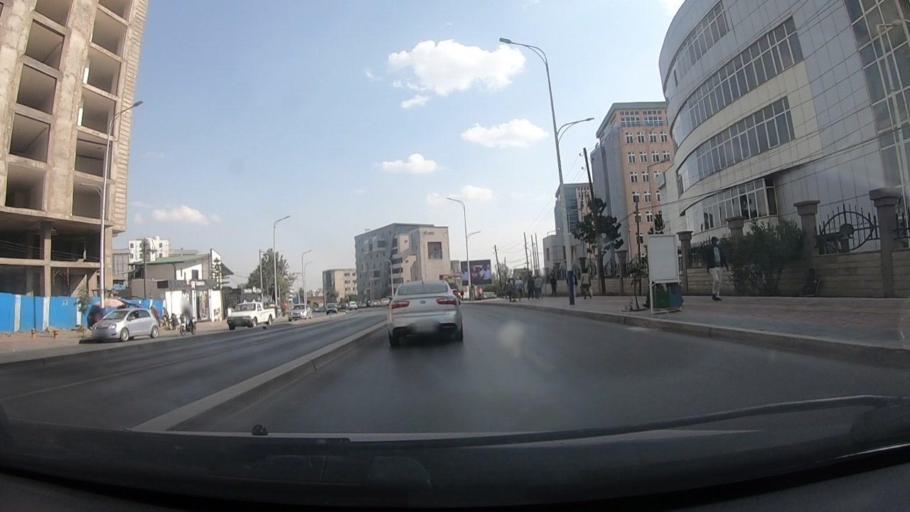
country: ET
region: Adis Abeba
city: Addis Ababa
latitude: 8.9920
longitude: 38.7396
